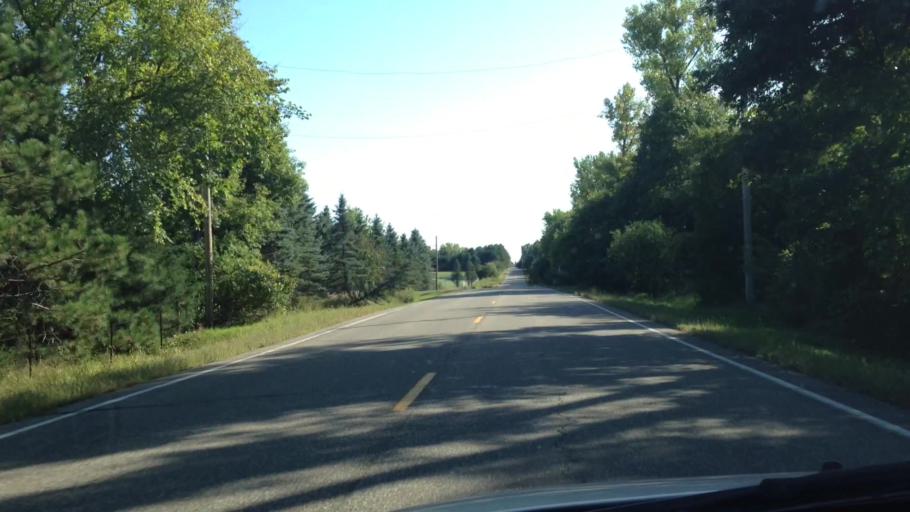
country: US
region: Minnesota
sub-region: Washington County
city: Stillwater
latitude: 45.1086
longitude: -92.8128
